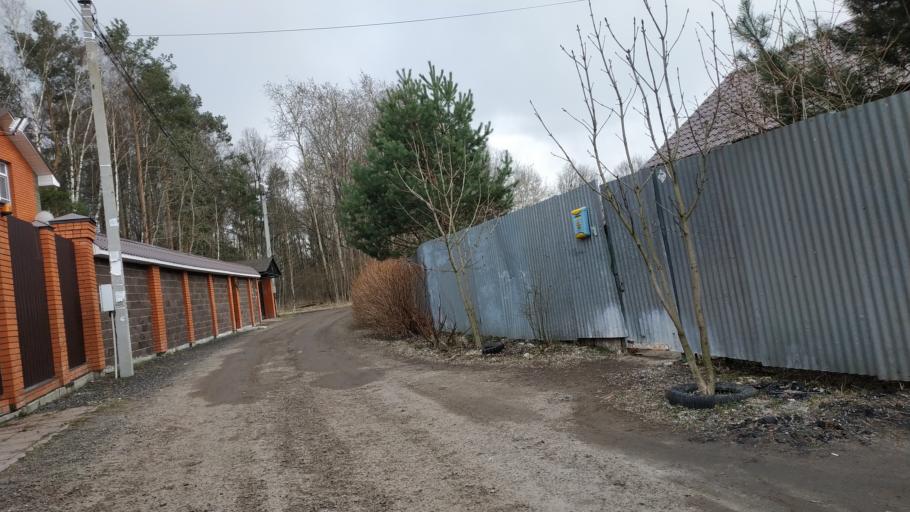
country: RU
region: Moskovskaya
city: Malyshevo
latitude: 55.5507
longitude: 38.3201
